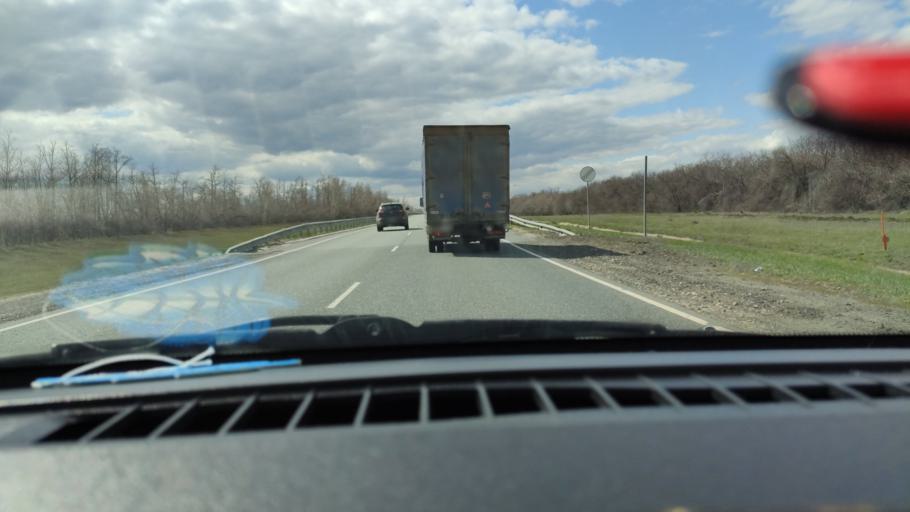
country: RU
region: Saratov
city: Balakovo
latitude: 52.1007
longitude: 47.7351
